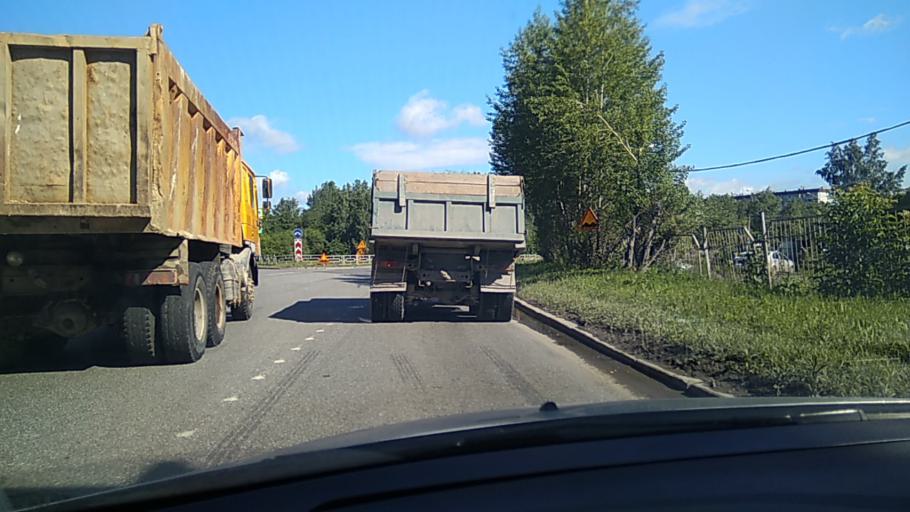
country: RU
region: Sverdlovsk
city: Sovkhoznyy
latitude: 56.8048
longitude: 60.5414
